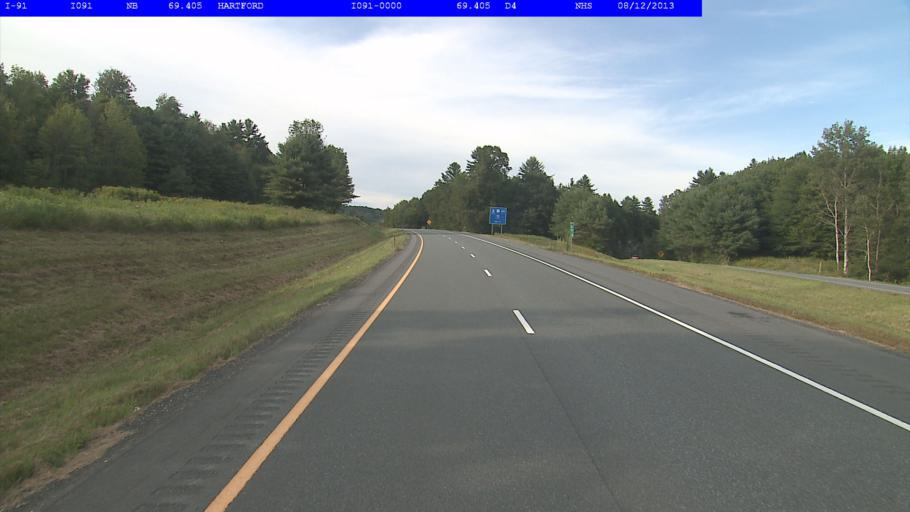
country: US
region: Vermont
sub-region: Windsor County
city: White River Junction
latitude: 43.6338
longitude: -72.3390
